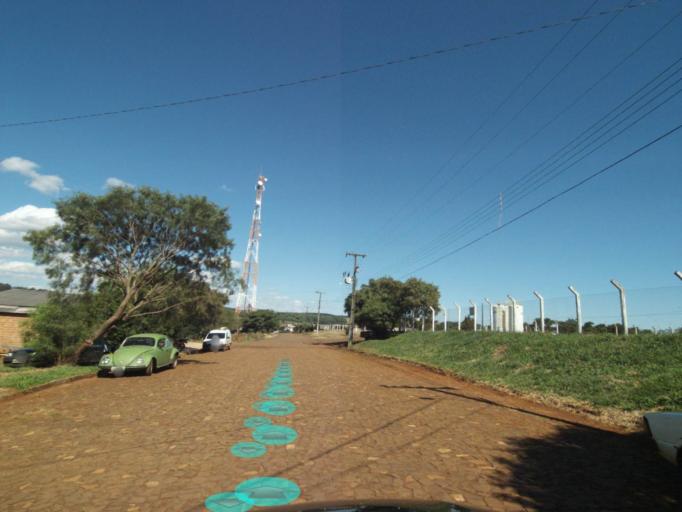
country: BR
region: Parana
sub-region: Coronel Vivida
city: Coronel Vivida
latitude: -26.1421
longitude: -52.3913
